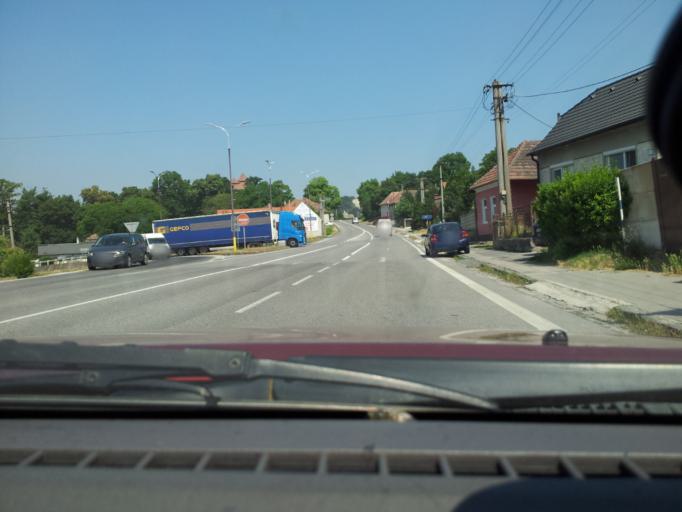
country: SK
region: Trnavsky
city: Smolenice
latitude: 48.5274
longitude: 17.4631
